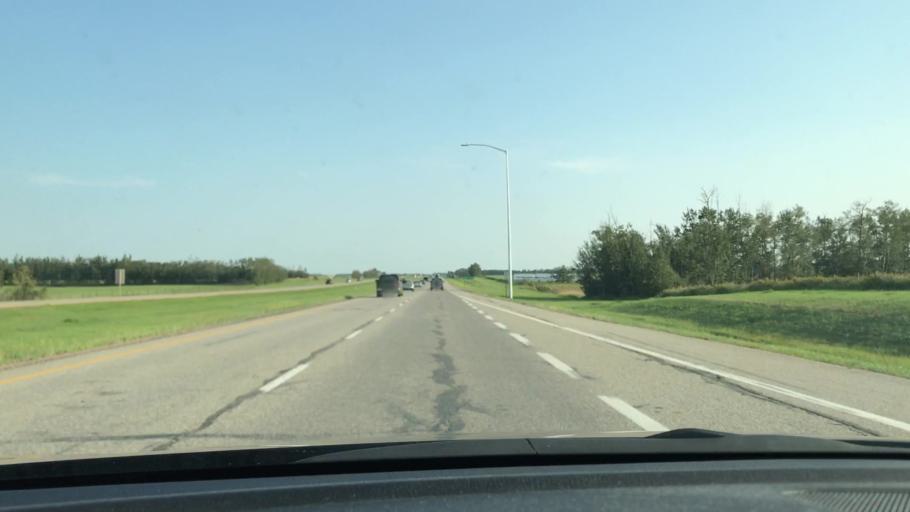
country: CA
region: Alberta
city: Millet
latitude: 53.0863
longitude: -113.5984
